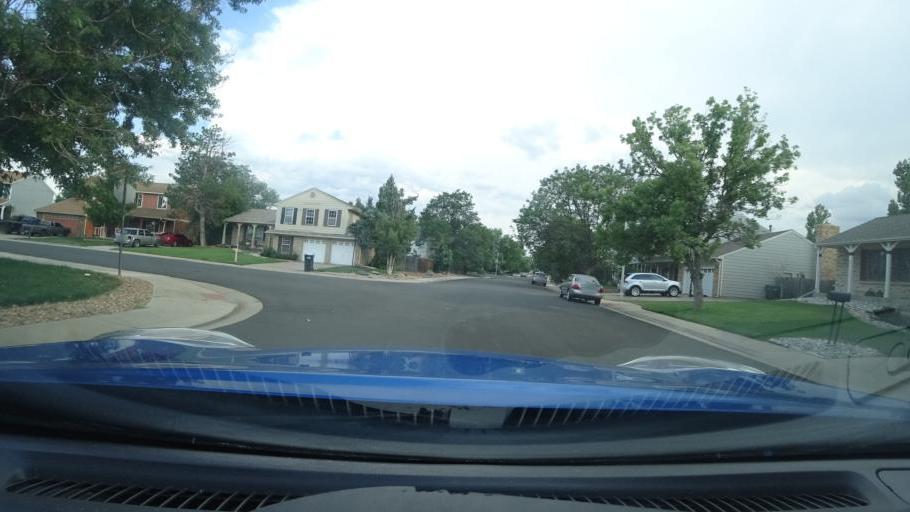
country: US
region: Colorado
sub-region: Adams County
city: Aurora
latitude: 39.6944
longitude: -104.8039
